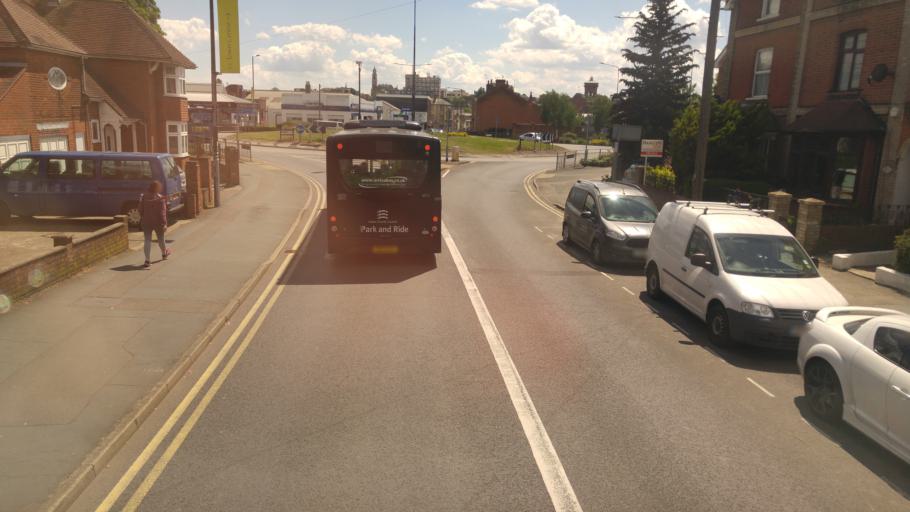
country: GB
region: England
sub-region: Essex
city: Colchester
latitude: 51.8979
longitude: 0.8953
